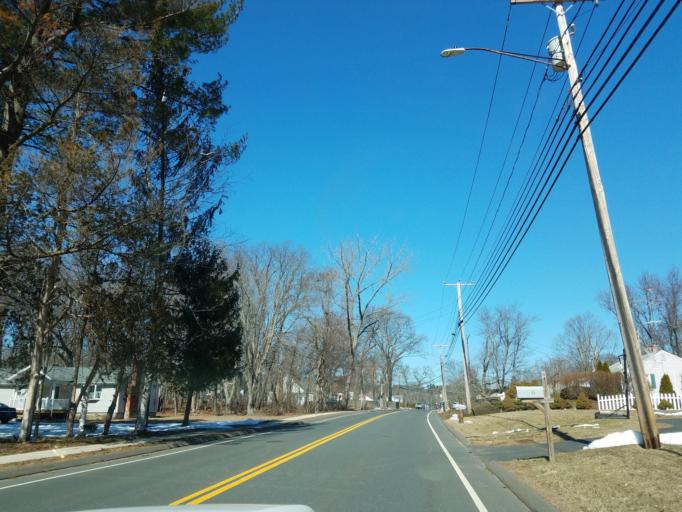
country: US
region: Connecticut
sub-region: Hartford County
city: Windsor Locks
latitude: 41.9098
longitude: -72.6366
